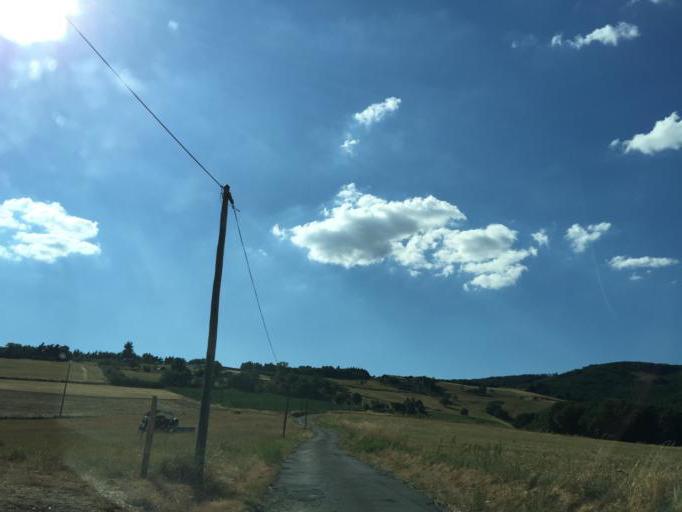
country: FR
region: Rhone-Alpes
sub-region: Departement de la Loire
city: Saint-Chamond
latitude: 45.5002
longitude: 4.5046
